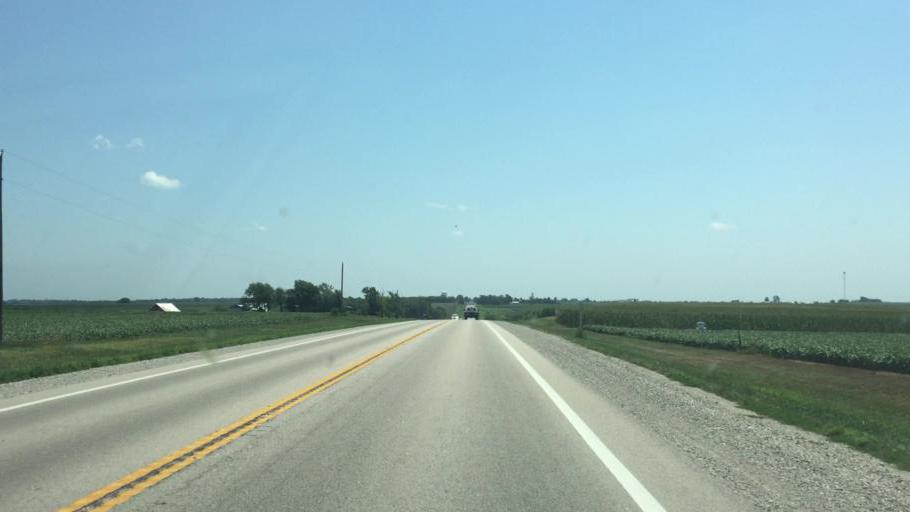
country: US
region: Kansas
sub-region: Brown County
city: Hiawatha
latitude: 39.8486
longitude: -95.5920
